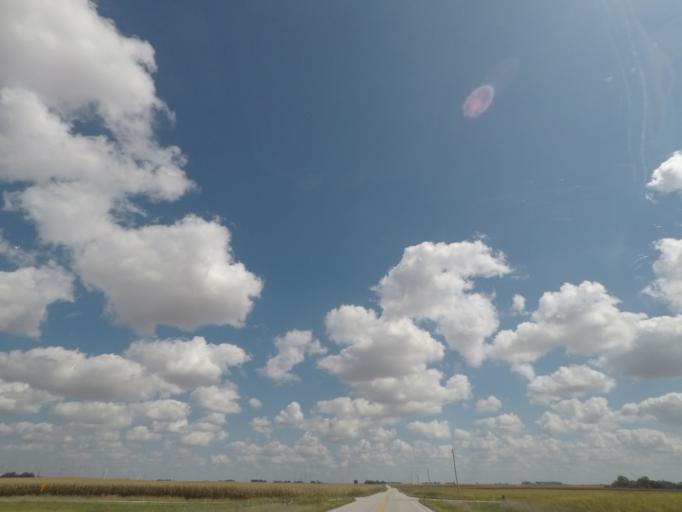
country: US
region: Iowa
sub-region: Story County
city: Nevada
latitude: 42.0777
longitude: -93.3519
